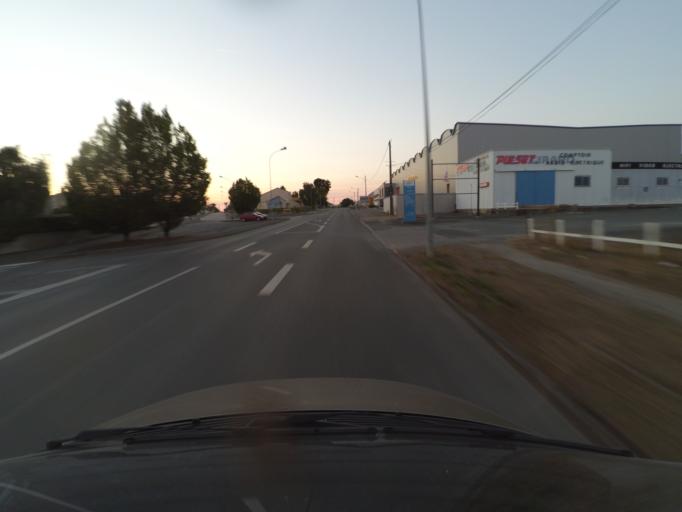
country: FR
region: Pays de la Loire
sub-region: Departement de la Vendee
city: La Roche-sur-Yon
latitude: 46.6543
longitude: -1.4456
